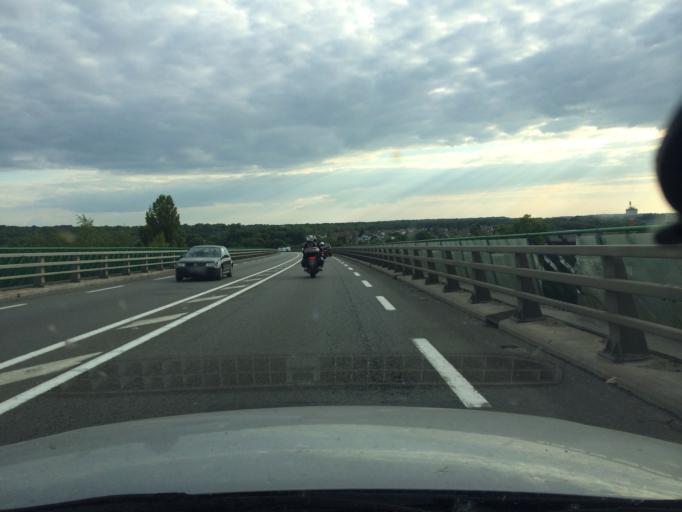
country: FR
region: Lorraine
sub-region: Departement de la Meuse
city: Ancerville
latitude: 48.6274
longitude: 4.9967
